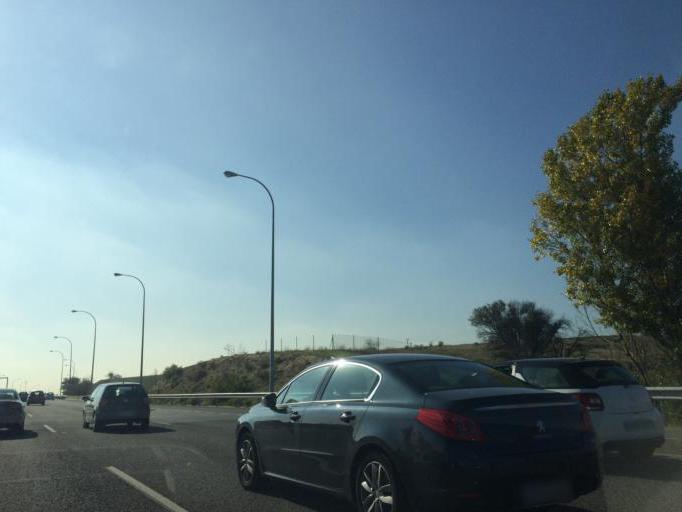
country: ES
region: Madrid
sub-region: Provincia de Madrid
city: Fuencarral-El Pardo
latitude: 40.5002
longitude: -3.7221
